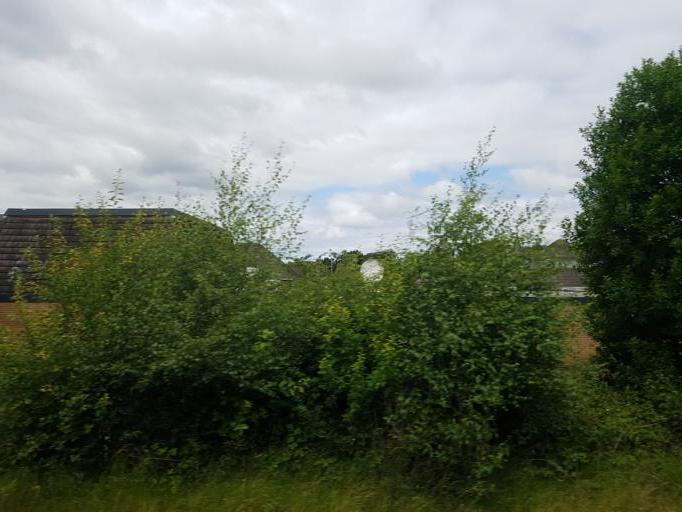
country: GB
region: Scotland
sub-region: East Dunbartonshire
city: Bishopbriggs
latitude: 55.9046
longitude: -4.2229
